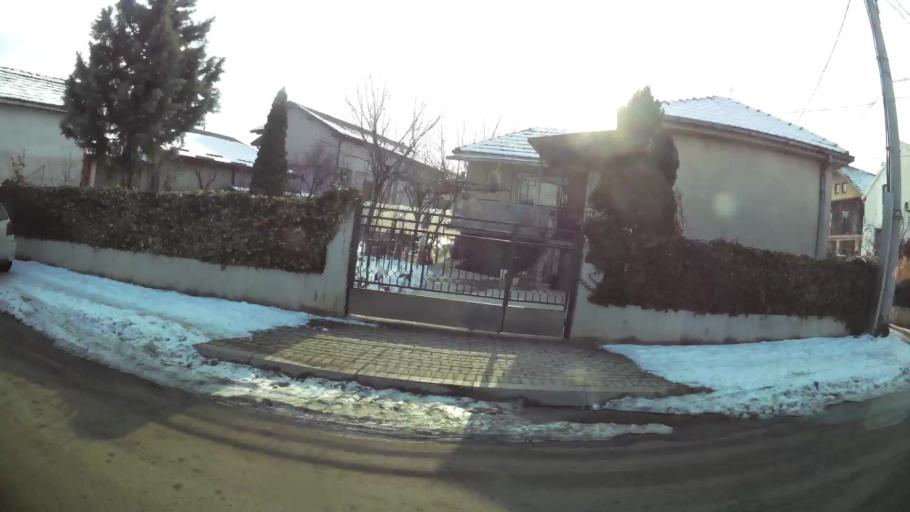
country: MK
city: Creshevo
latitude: 42.0121
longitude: 21.4972
